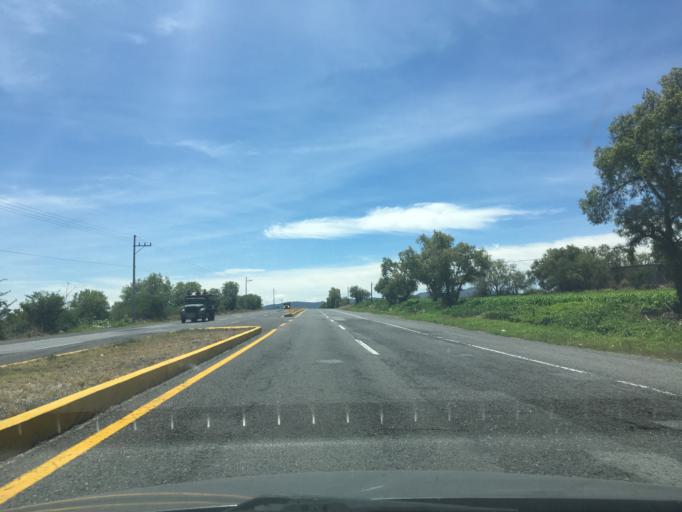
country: MX
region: Hidalgo
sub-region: Alfajayucan
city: Santa Maria Xigui
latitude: 20.4346
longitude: -99.4057
